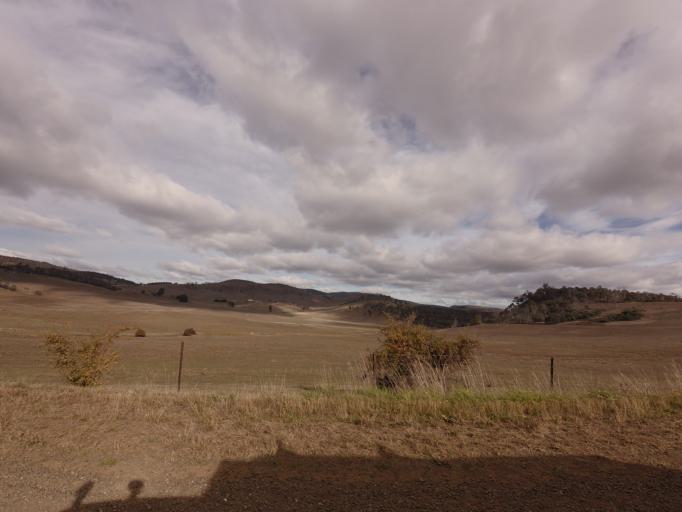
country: AU
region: Tasmania
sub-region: Brighton
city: Bridgewater
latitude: -42.4611
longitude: 147.2746
